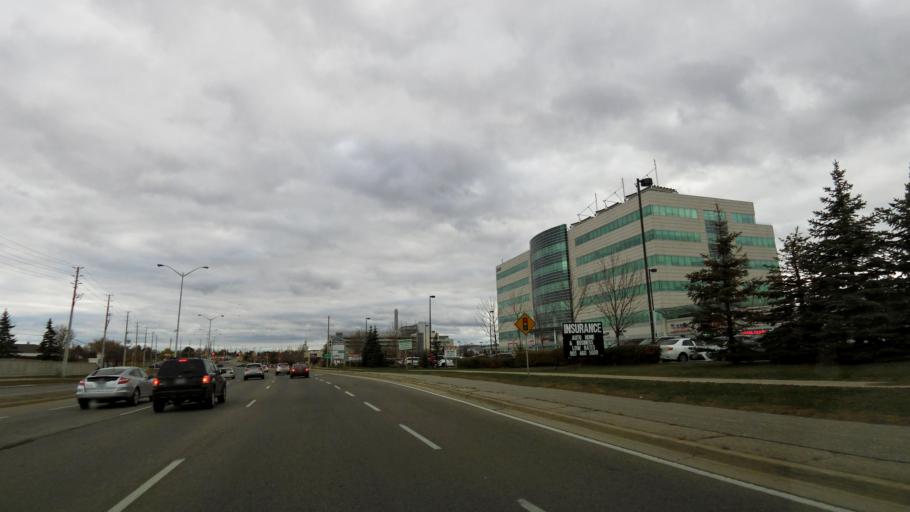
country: CA
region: Ontario
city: Brampton
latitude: 43.7511
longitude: -79.7380
